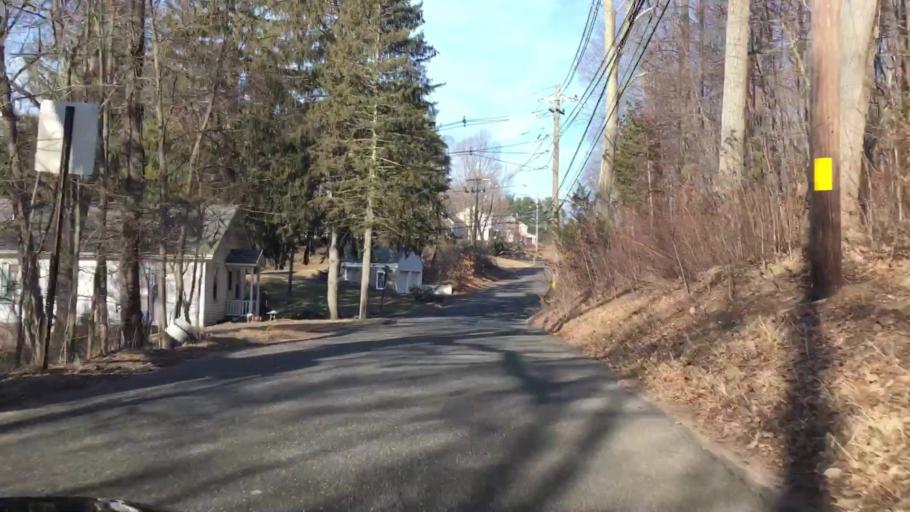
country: US
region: Connecticut
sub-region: New Haven County
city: Meriden
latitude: 41.5123
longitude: -72.7570
